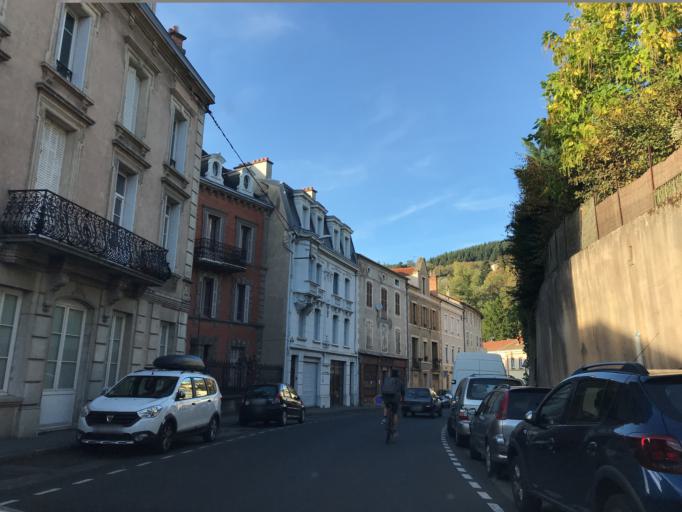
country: FR
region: Auvergne
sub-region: Departement du Puy-de-Dome
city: Thiers
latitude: 45.8589
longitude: 3.5459
